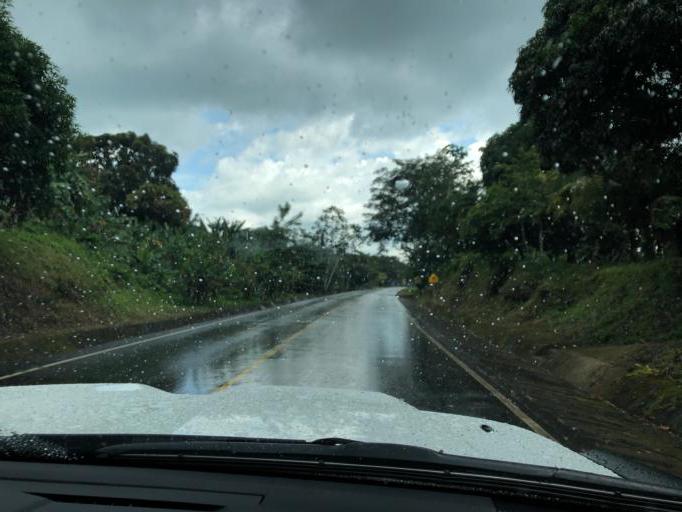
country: NI
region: Chontales
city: Villa Sandino
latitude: 12.0218
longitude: -84.9535
